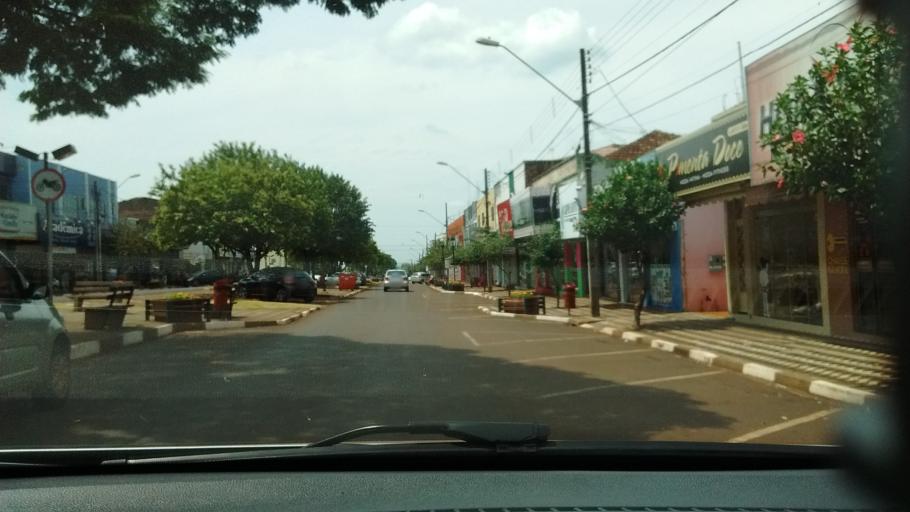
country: BR
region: Parana
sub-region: Corbelia
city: Corbelia
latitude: -24.5425
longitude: -52.9899
